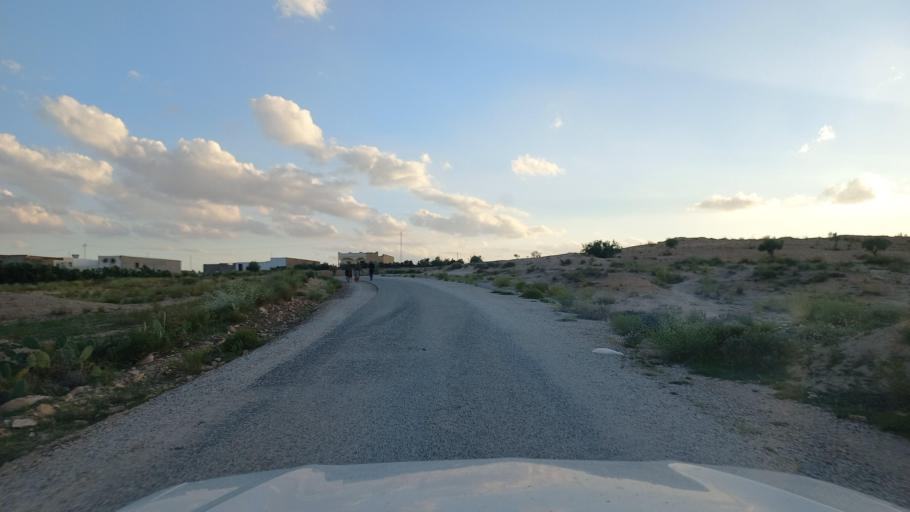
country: TN
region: Al Qasrayn
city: Sbiba
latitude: 35.3745
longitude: 9.0621
